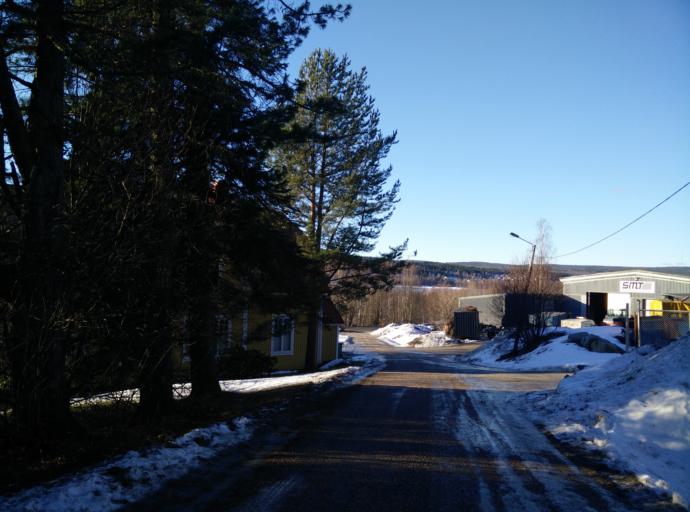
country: SE
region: Vaesternorrland
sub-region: Sundsvalls Kommun
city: Skottsund
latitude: 62.3141
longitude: 17.3950
